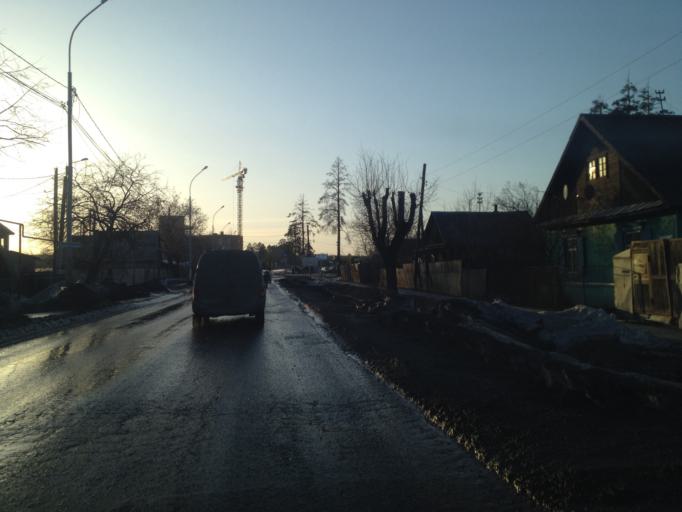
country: RU
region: Sverdlovsk
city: Sovkhoznyy
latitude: 56.7646
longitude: 60.5589
